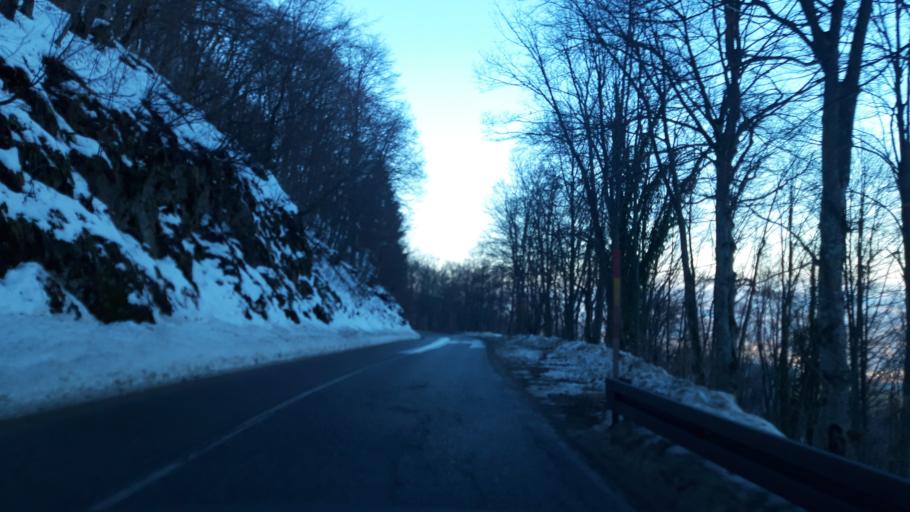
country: BA
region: Republika Srpska
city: Vlasenica
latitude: 44.1548
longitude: 18.9426
